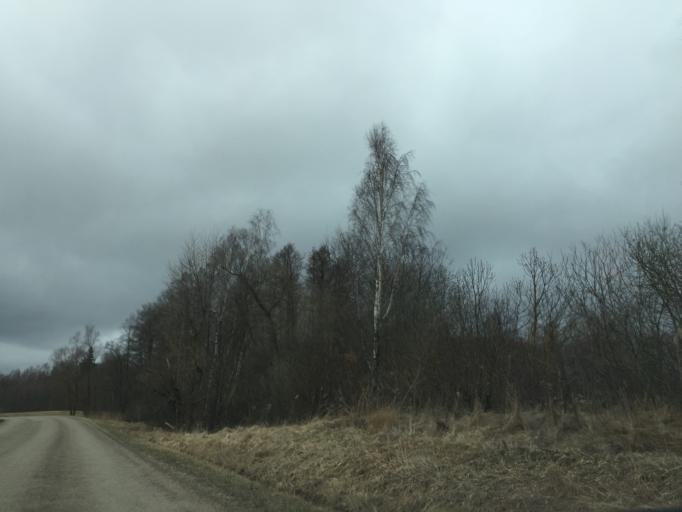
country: LV
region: Ilukste
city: Ilukste
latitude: 56.0177
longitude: 26.2455
